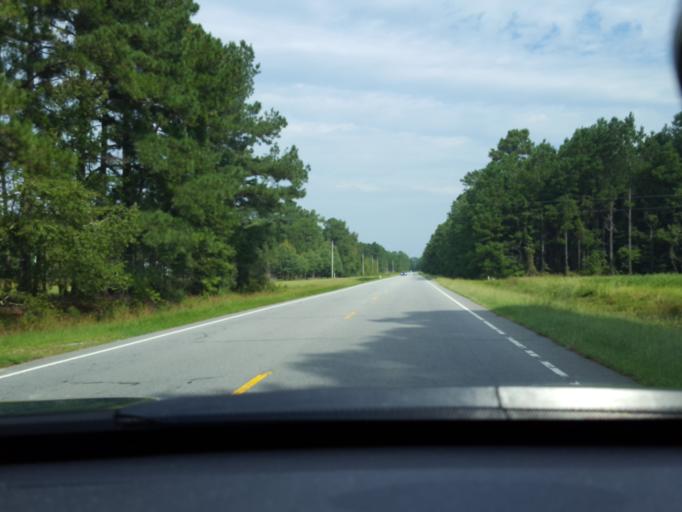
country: US
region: North Carolina
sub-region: Washington County
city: Plymouth
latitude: 35.9515
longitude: -76.7463
